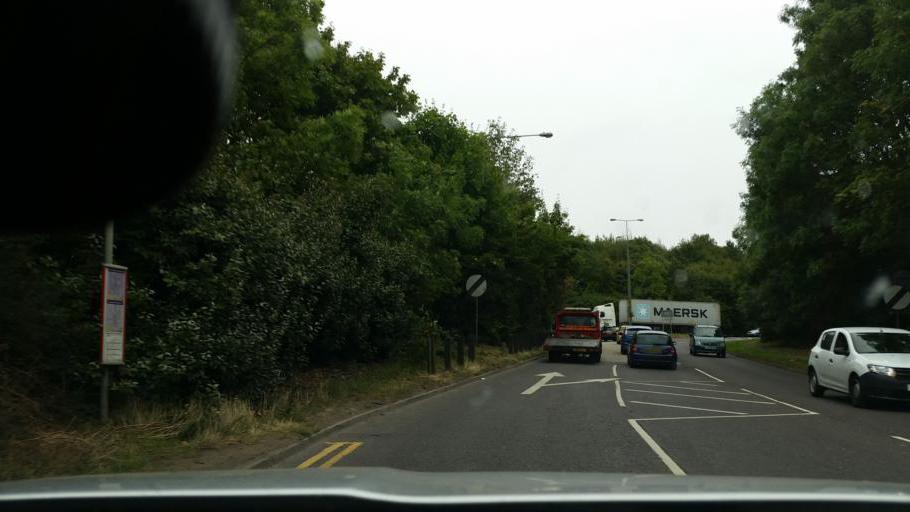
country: GB
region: England
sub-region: Kent
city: Swanley
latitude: 51.3880
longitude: 0.1906
